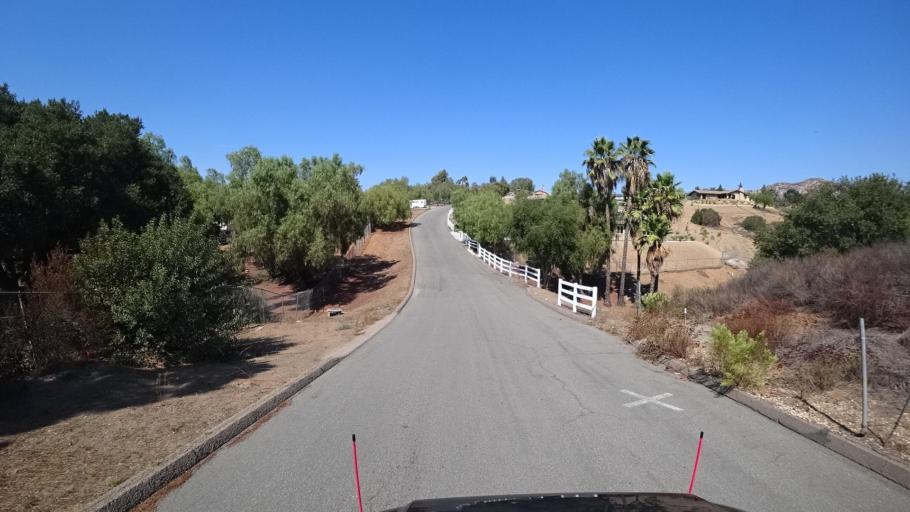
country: US
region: California
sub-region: San Diego County
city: Granite Hills
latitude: 32.7822
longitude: -116.8975
